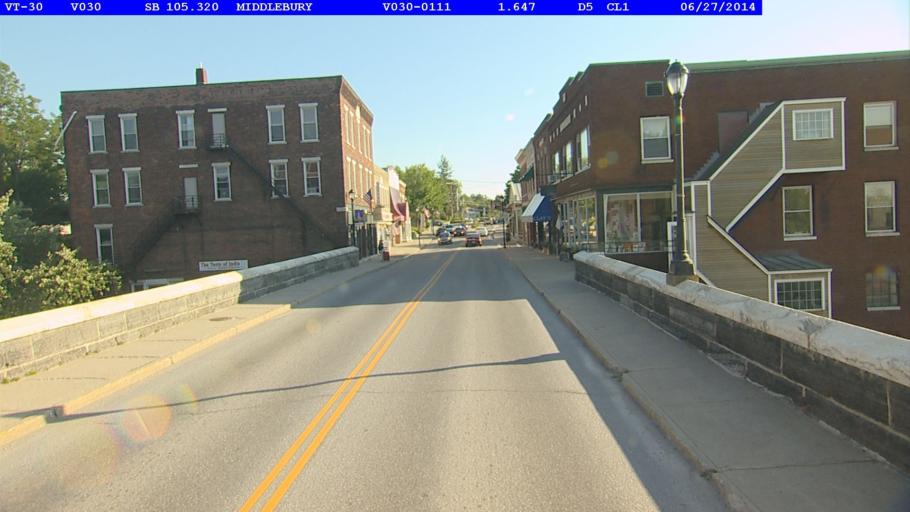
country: US
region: Vermont
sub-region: Addison County
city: Middlebury (village)
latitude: 44.0134
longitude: -73.1686
